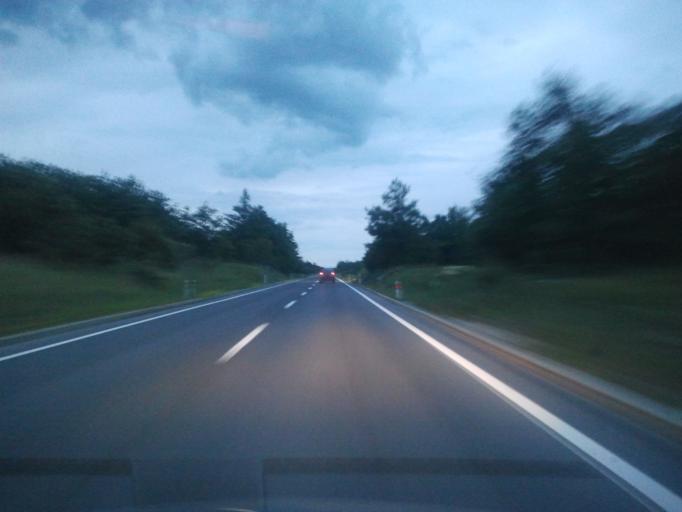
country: HR
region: Zadarska
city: Gracac
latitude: 44.4558
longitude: 15.8245
